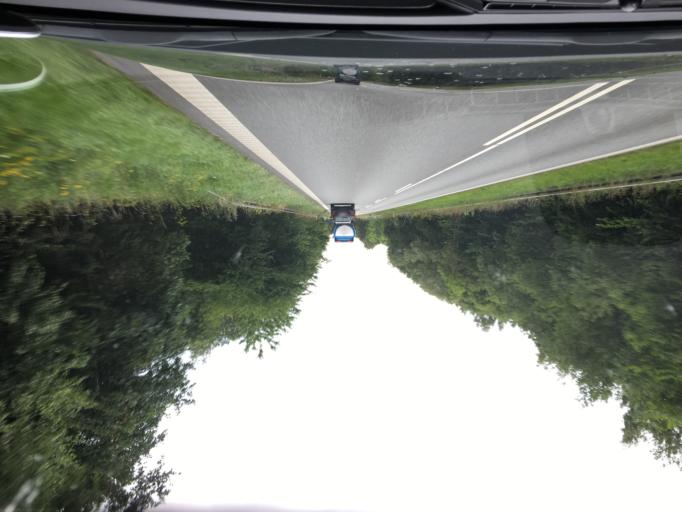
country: DK
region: Capital Region
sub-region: Hillerod Kommune
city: Nodebo
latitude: 55.9390
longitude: 12.3551
